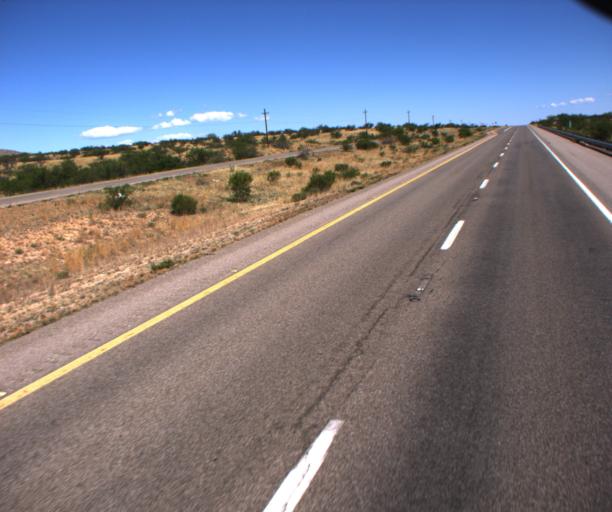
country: US
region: Arizona
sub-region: Cochise County
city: Whetstone
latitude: 31.8558
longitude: -110.3410
